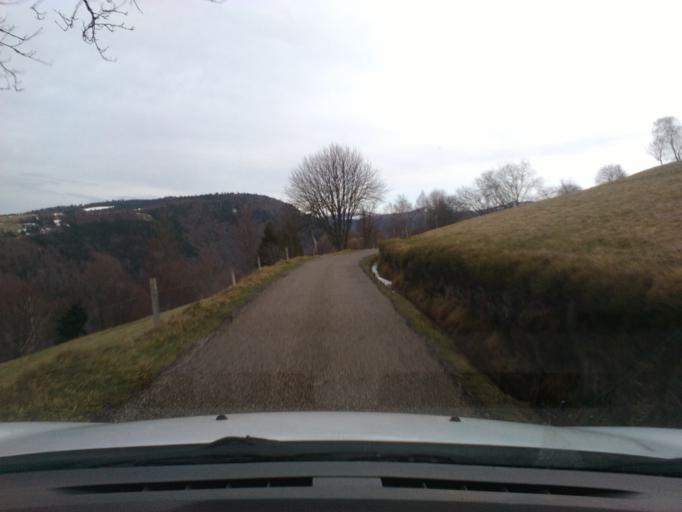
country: FR
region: Lorraine
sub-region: Departement des Vosges
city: La Bresse
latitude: 47.9971
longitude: 6.8875
